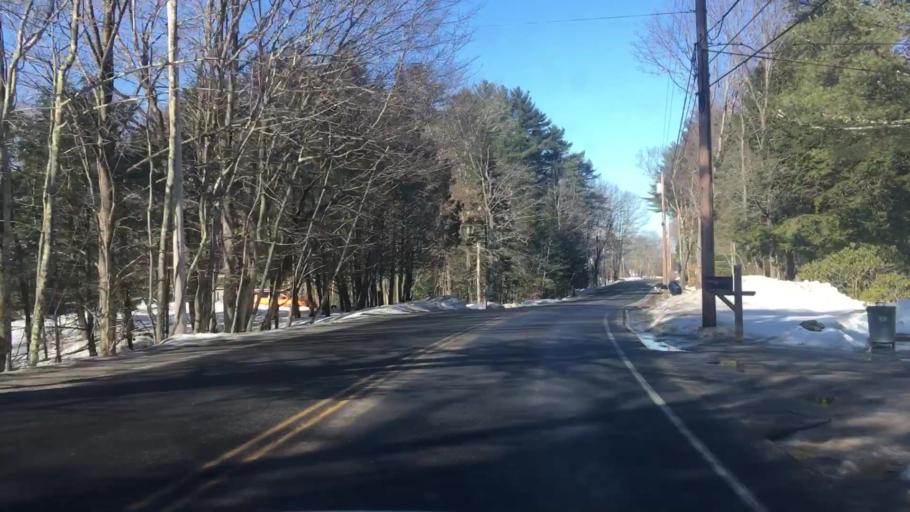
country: US
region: Maine
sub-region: Cumberland County
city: North Windham
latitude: 43.8159
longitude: -70.3835
